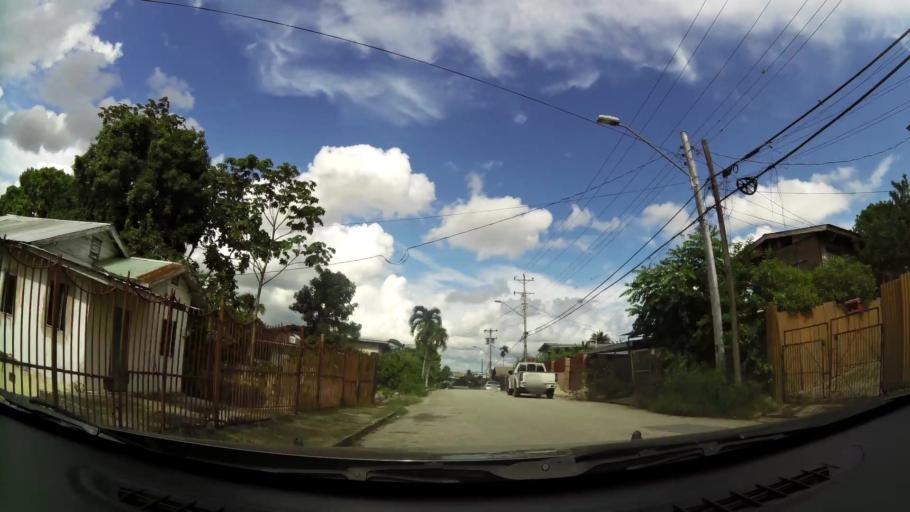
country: TT
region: City of San Fernando
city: Mon Repos
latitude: 10.2746
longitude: -61.4499
